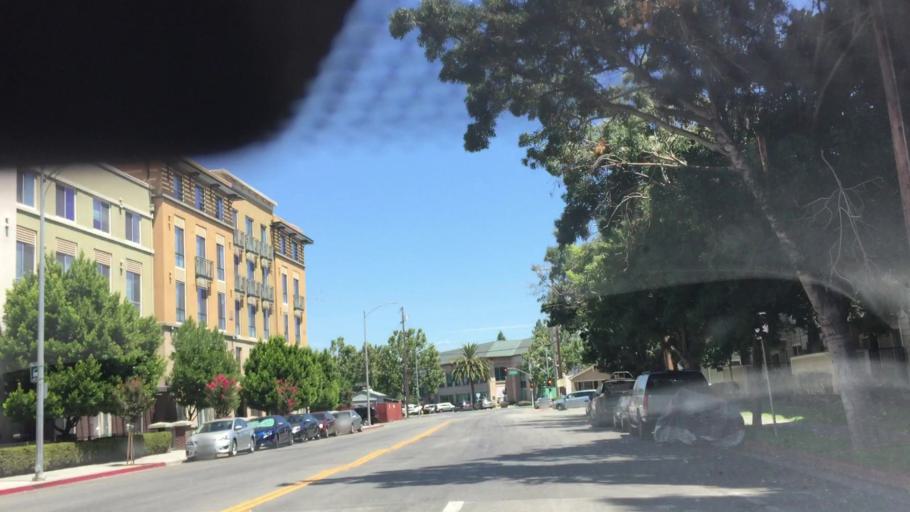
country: US
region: California
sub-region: Santa Clara County
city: Buena Vista
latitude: 37.3167
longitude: -121.9092
